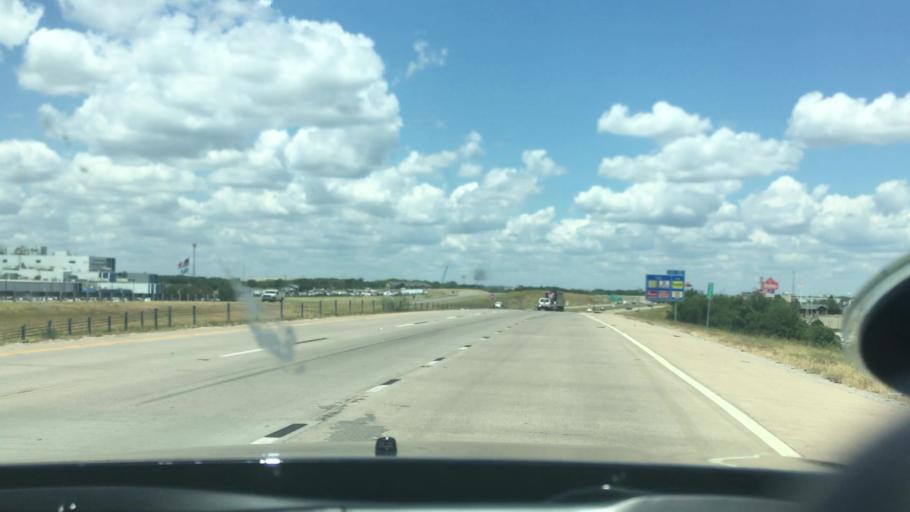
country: US
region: Oklahoma
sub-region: Carter County
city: Ardmore
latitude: 34.1776
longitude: -97.1678
